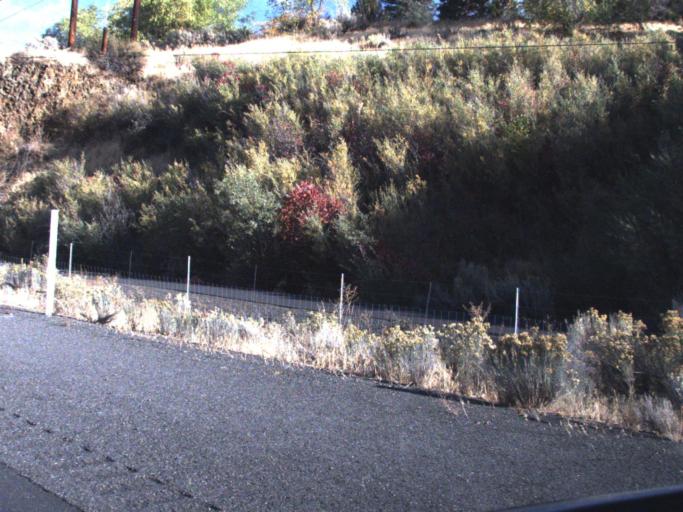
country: US
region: Washington
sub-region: Yakima County
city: Gleed
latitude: 46.6951
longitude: -120.6531
